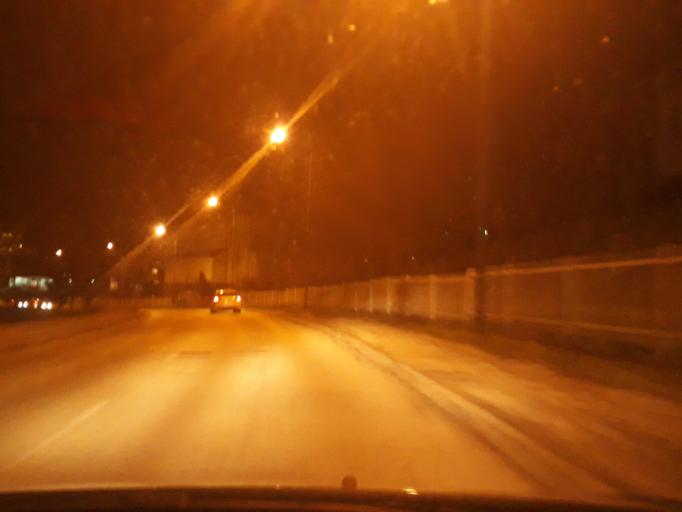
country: BA
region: Federation of Bosnia and Herzegovina
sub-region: Kanton Sarajevo
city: Sarajevo
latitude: 43.8374
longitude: 18.3483
